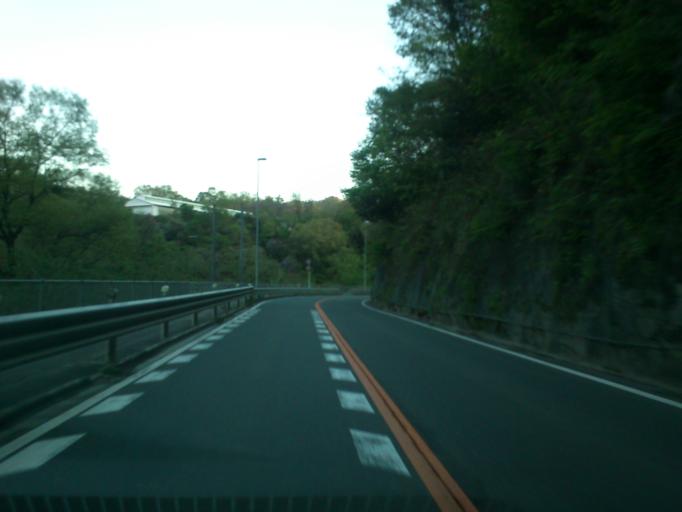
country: JP
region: Kyoto
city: Ayabe
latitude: 35.2066
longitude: 135.4241
